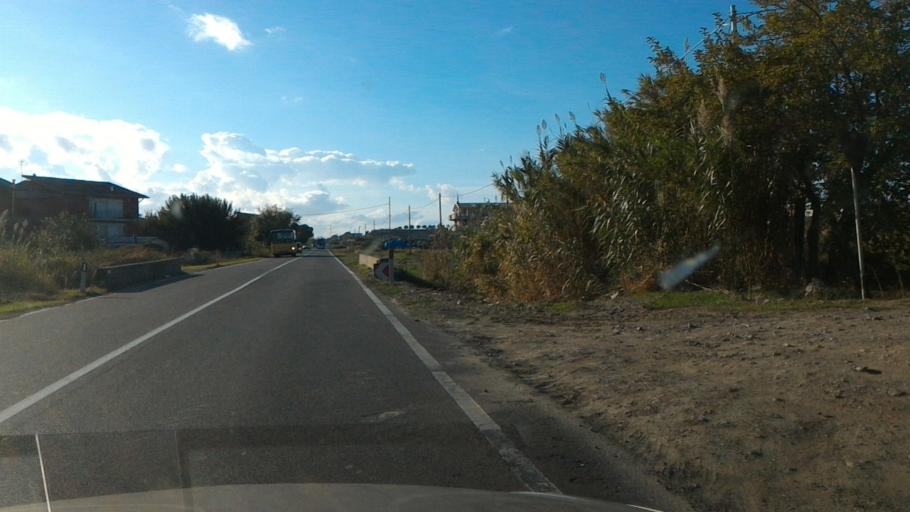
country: IT
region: Calabria
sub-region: Provincia di Crotone
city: Tronca
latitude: 39.2204
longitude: 17.1040
